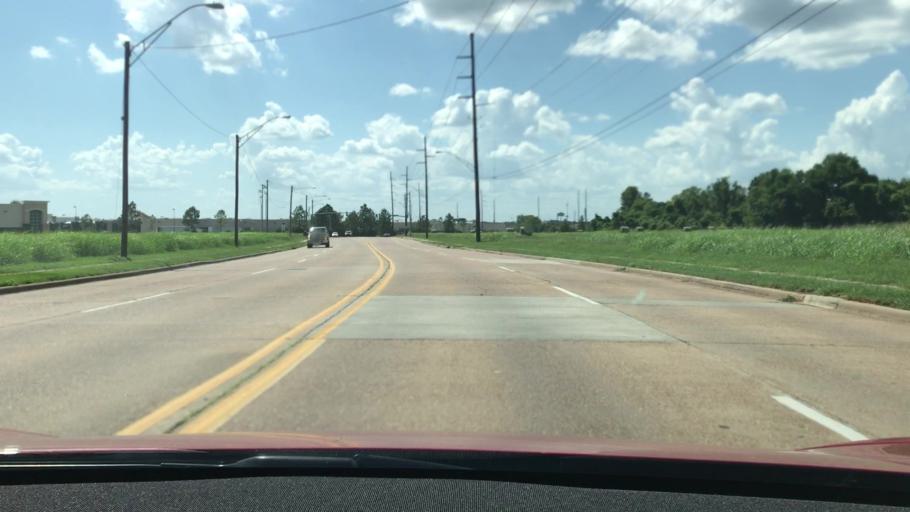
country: US
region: Louisiana
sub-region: Bossier Parish
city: Bossier City
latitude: 32.4400
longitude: -93.7091
